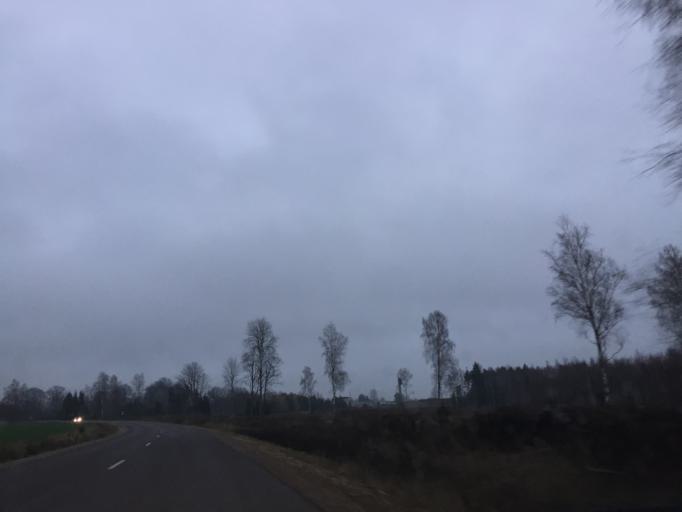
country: LV
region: Koceni
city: Koceni
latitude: 57.5500
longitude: 25.3709
